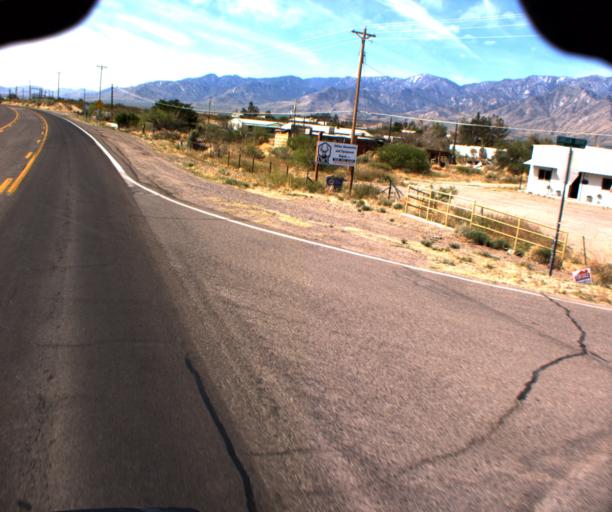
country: US
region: Arizona
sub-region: Graham County
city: Cactus Flat
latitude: 32.7787
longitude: -109.7160
